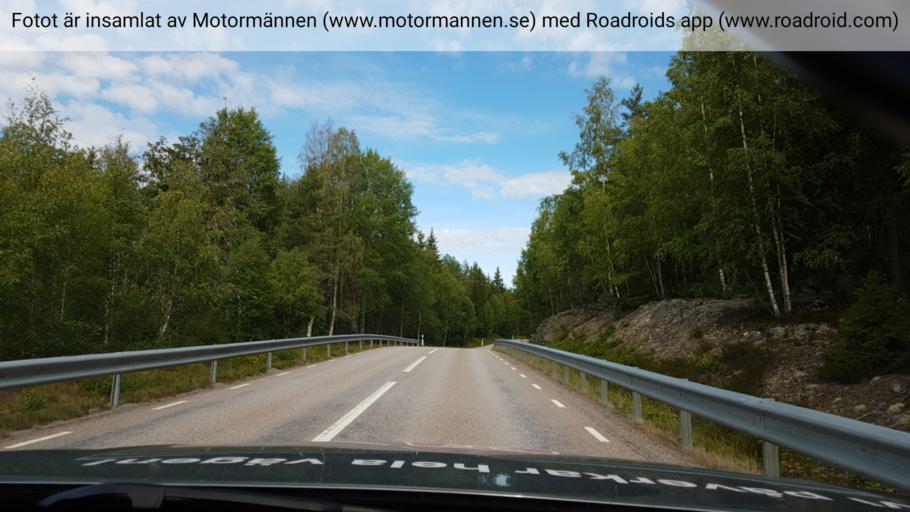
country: SE
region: Uppsala
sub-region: Heby Kommun
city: OEstervala
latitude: 60.0065
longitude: 17.2980
